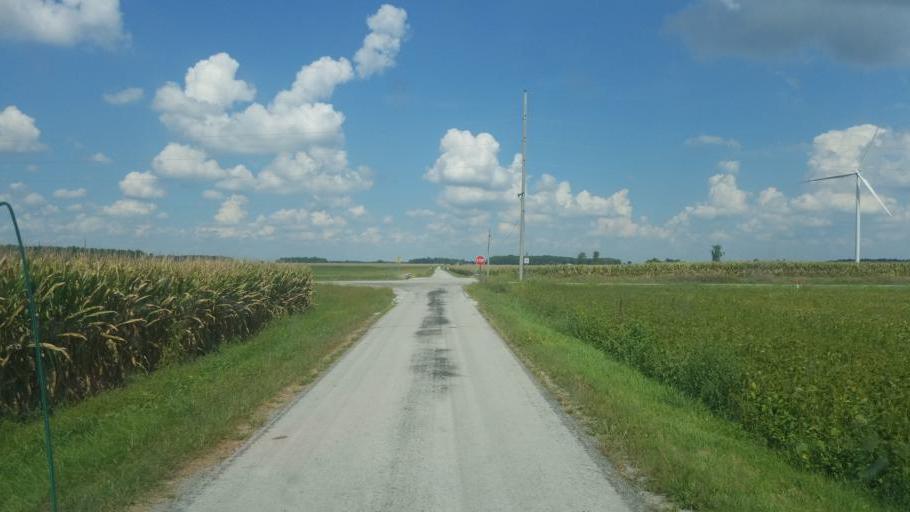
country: US
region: Ohio
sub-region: Hardin County
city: Ada
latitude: 40.7902
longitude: -83.7478
